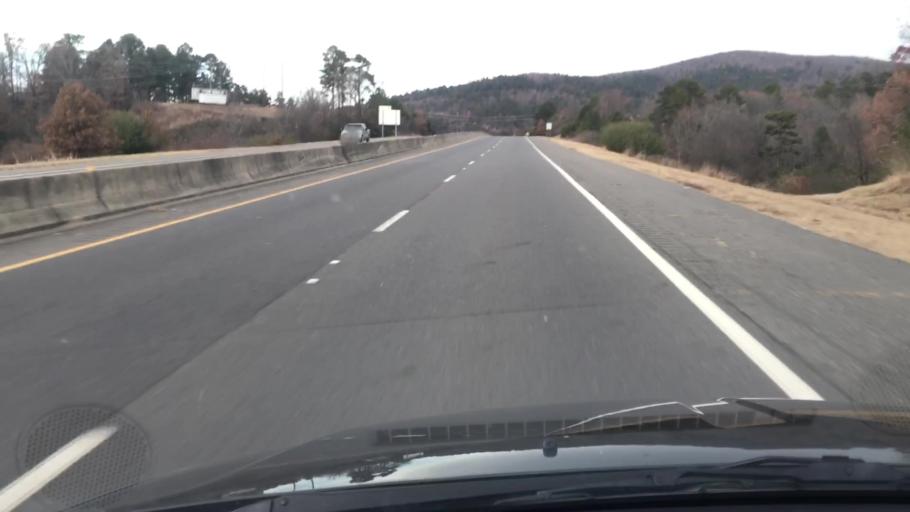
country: US
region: Arkansas
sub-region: Garland County
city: Piney
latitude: 34.4862
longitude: -93.1120
